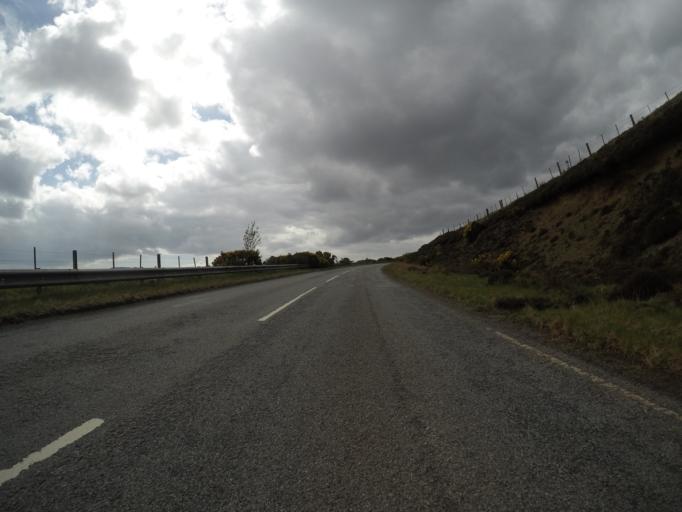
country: GB
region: Scotland
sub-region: Highland
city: Isle of Skye
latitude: 57.3044
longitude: -6.3032
